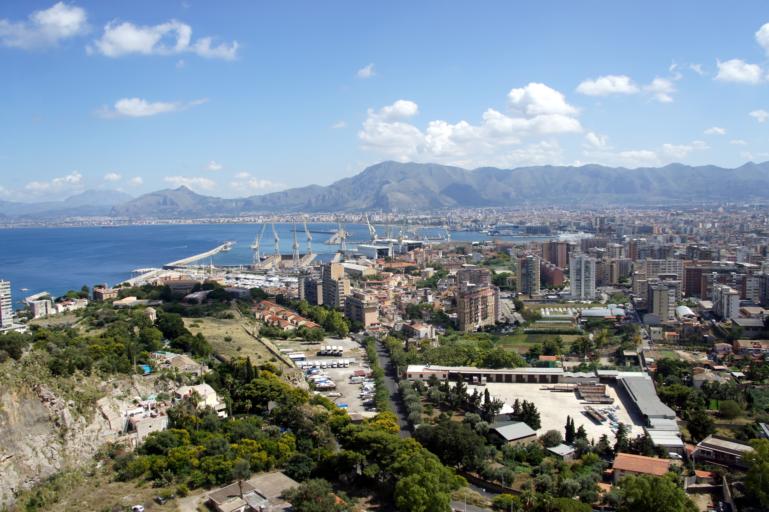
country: IT
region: Sicily
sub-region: Palermo
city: Palermo
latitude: 38.1520
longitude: 13.3641
